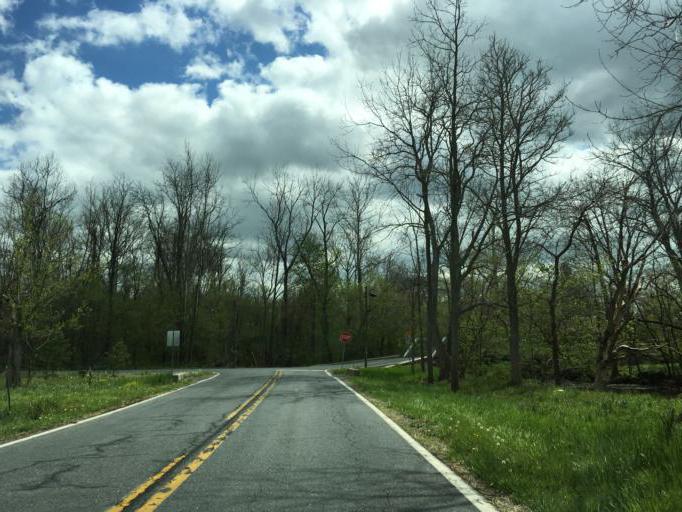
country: US
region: Maryland
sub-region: Frederick County
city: Thurmont
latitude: 39.5700
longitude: -77.3914
